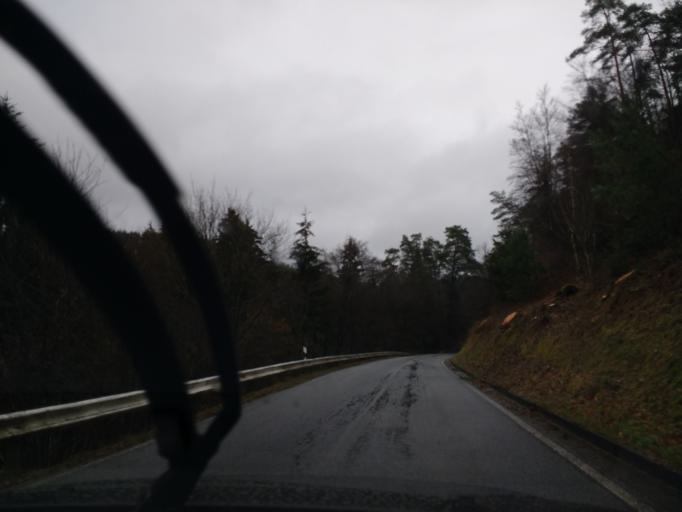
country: DE
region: Rheinland-Pfalz
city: Rascheid
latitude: 49.7257
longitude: 6.9397
